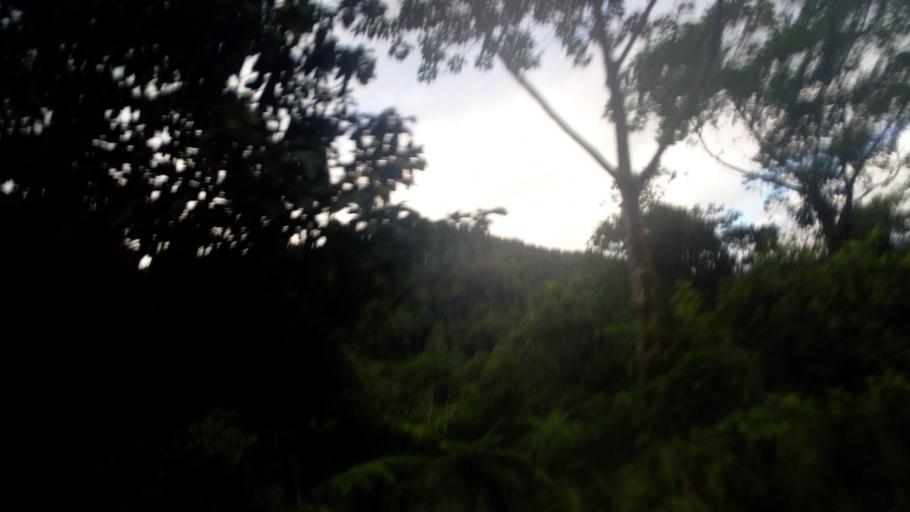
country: AU
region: Queensland
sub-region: Tablelands
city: Ravenshoe
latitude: -17.5617
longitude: 145.6869
